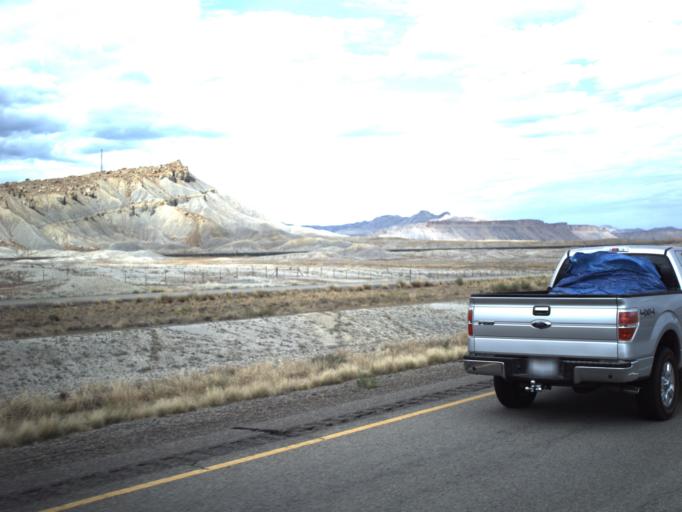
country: US
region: Utah
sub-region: Grand County
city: Moab
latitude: 38.9311
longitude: -109.8689
